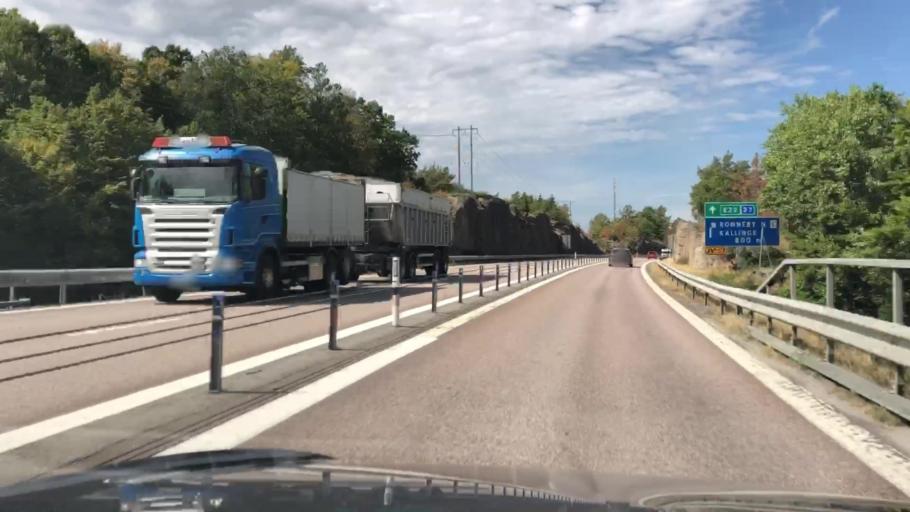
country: SE
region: Blekinge
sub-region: Ronneby Kommun
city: Ronneby
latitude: 56.2152
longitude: 15.2968
